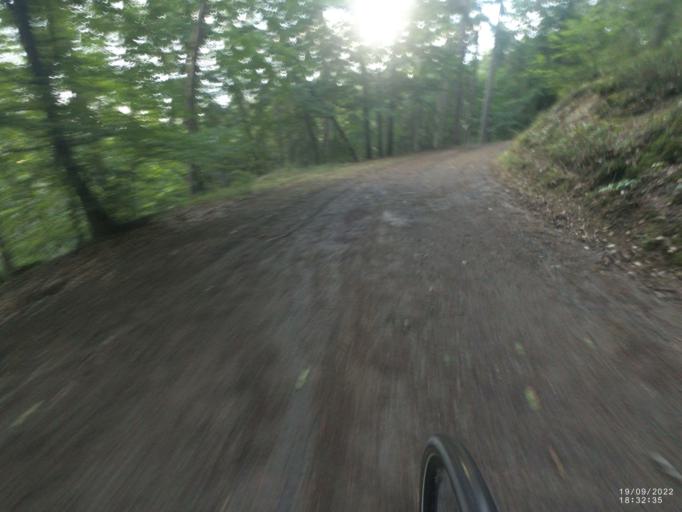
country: DE
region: Rheinland-Pfalz
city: Schalkenmehren
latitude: 50.1554
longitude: 6.8428
